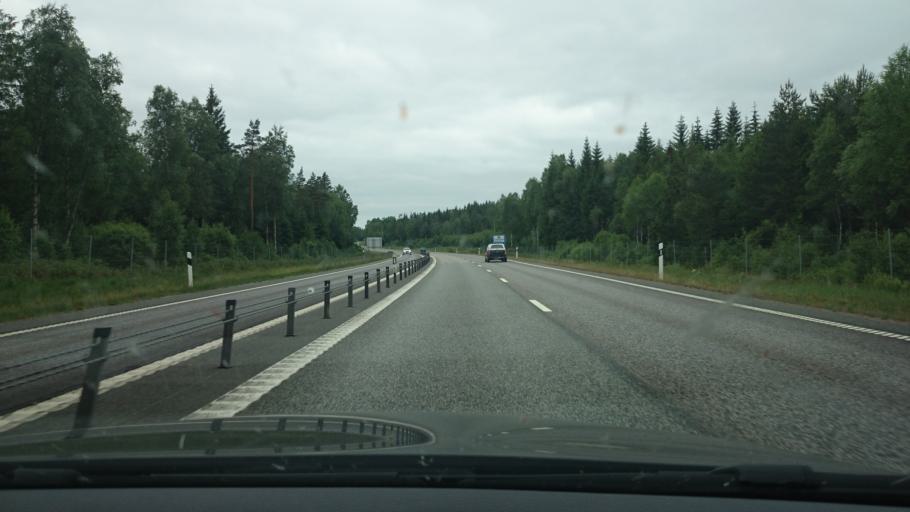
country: SE
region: Halland
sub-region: Hylte Kommun
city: Hyltebruk
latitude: 56.9763
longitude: 13.1809
